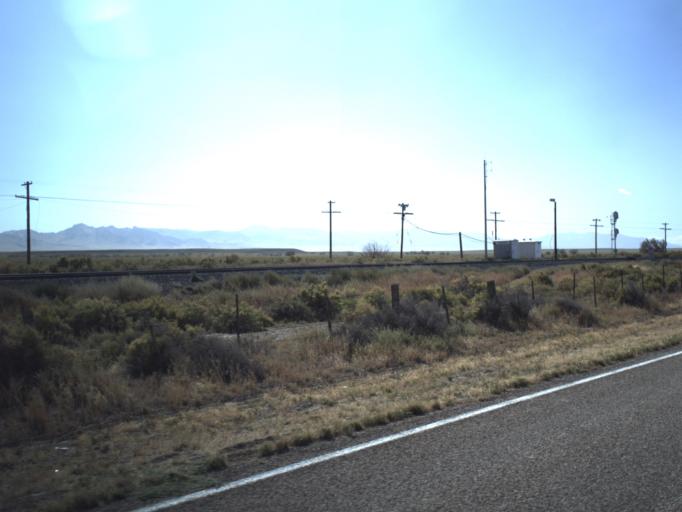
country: US
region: Utah
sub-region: Beaver County
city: Milford
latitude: 38.7096
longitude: -112.9701
